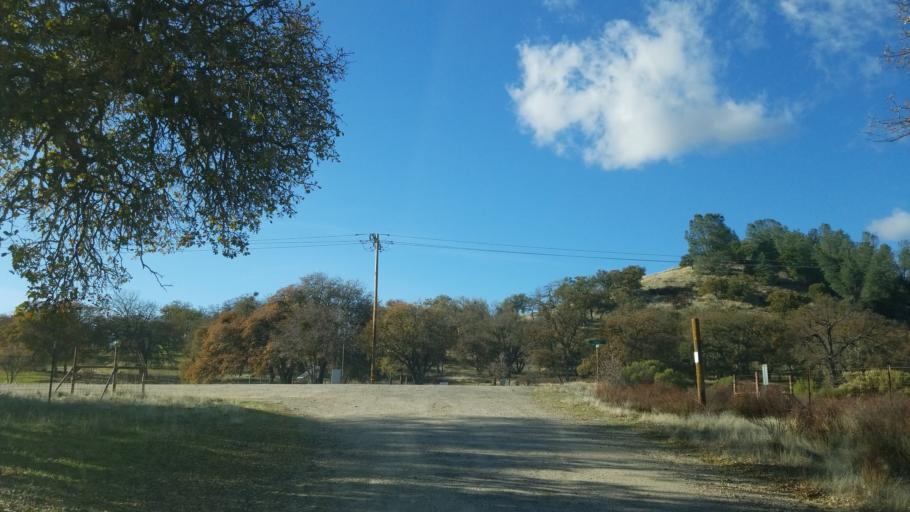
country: US
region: California
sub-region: Monterey County
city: King City
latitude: 35.9716
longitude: -121.1753
